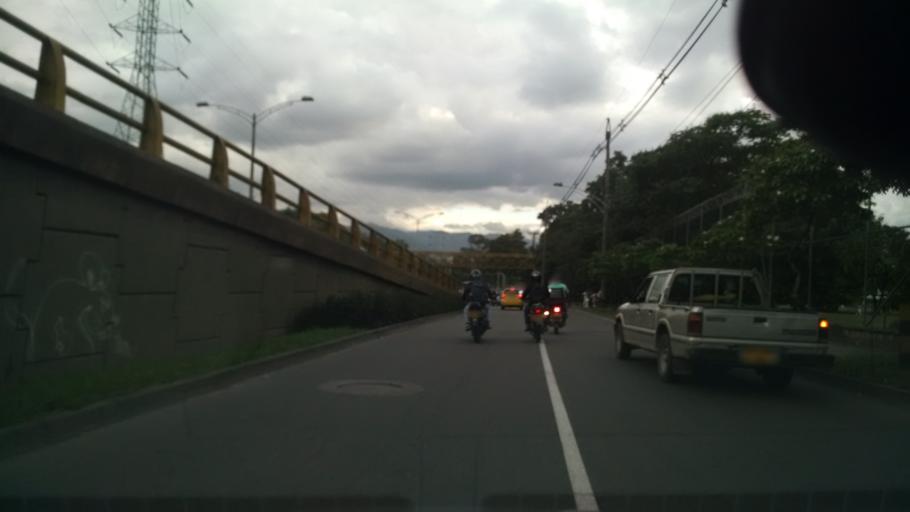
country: CO
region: Antioquia
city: Medellin
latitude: 6.2649
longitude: -75.5752
